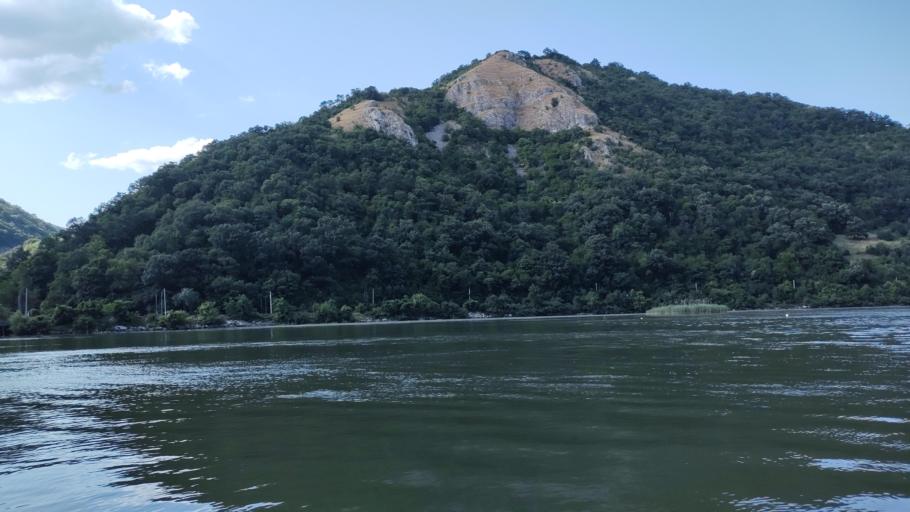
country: RO
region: Caras-Severin
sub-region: Comuna Pescari
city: Coronini
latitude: 44.6559
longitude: 21.7432
